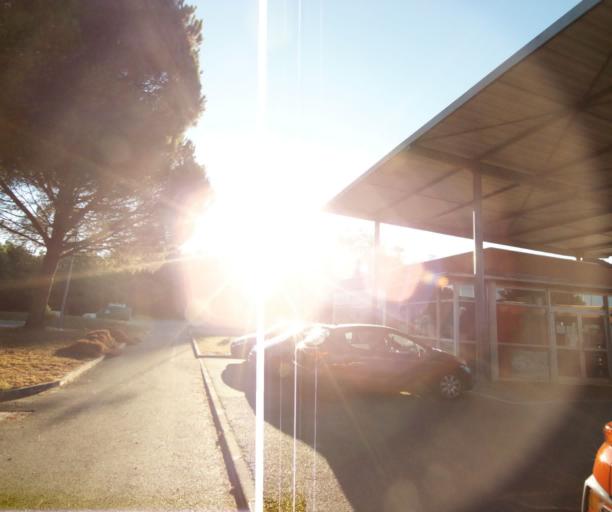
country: FR
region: Midi-Pyrenees
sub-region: Departement de la Haute-Garonne
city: Castanet-Tolosan
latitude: 43.5211
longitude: 1.5171
